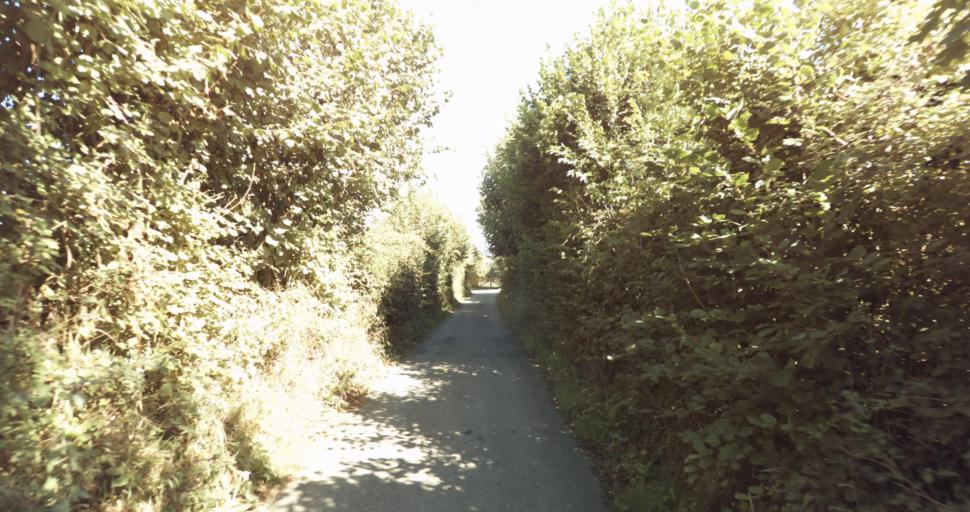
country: FR
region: Lower Normandy
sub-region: Departement de l'Orne
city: Gace
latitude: 48.8025
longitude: 0.2161
